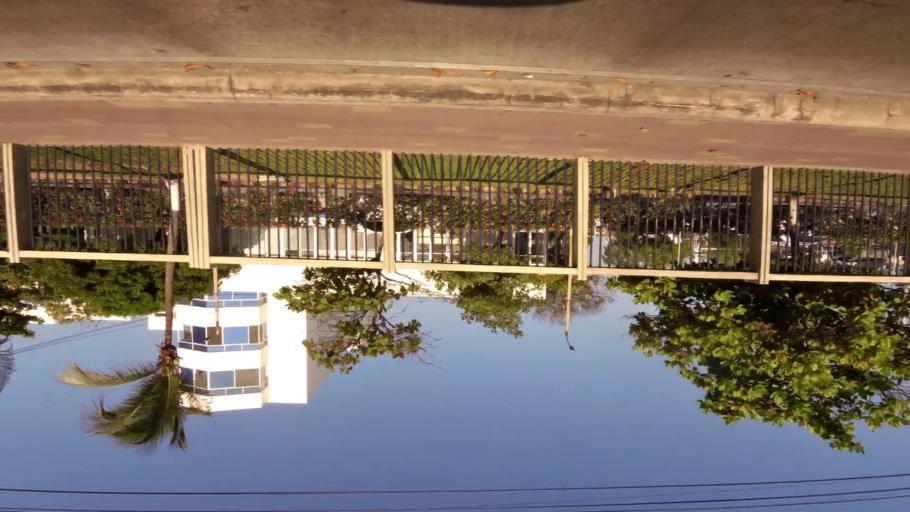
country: CO
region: Bolivar
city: Cartagena
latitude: 10.4167
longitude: -75.5512
